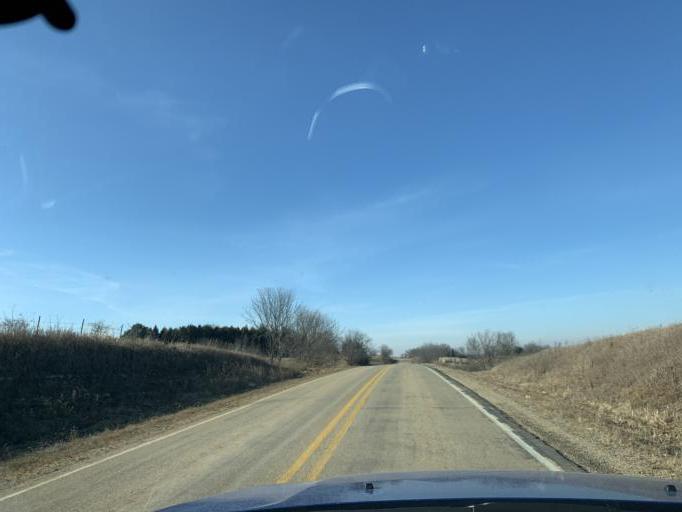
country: US
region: Wisconsin
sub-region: Iowa County
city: Barneveld
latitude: 42.8109
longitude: -89.8932
